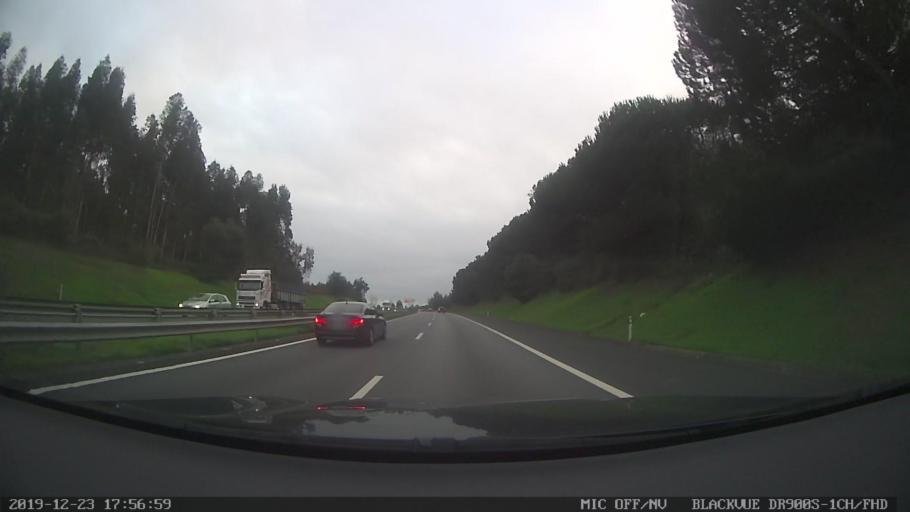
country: PT
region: Aveiro
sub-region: Mealhada
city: Mealhada
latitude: 40.3432
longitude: -8.4960
